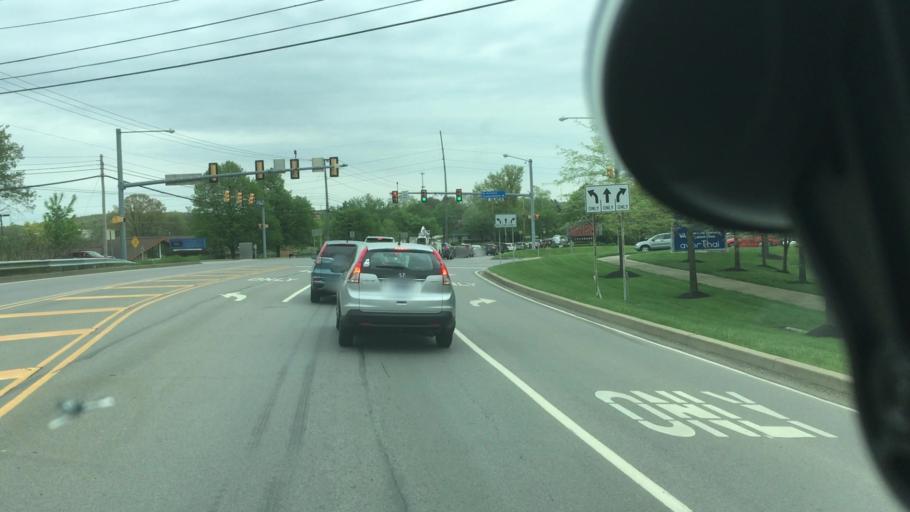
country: US
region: Pennsylvania
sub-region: Butler County
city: Cranberry Township
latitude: 40.6841
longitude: -80.1122
